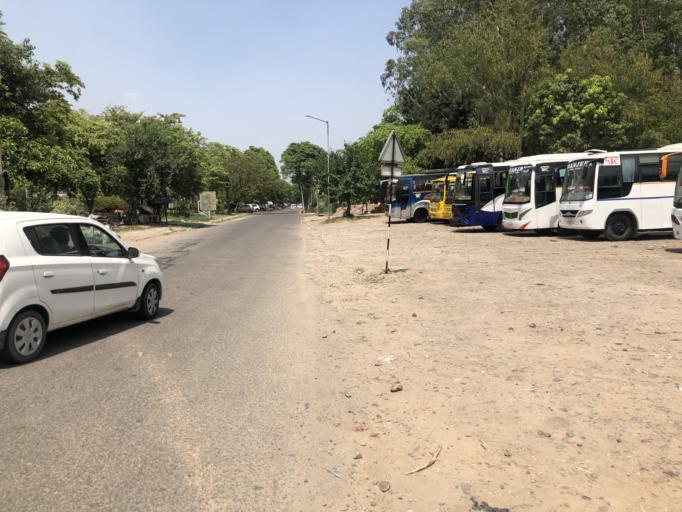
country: IN
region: Punjab
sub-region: Ajitgarh
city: Mohali
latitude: 30.7098
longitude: 76.7485
